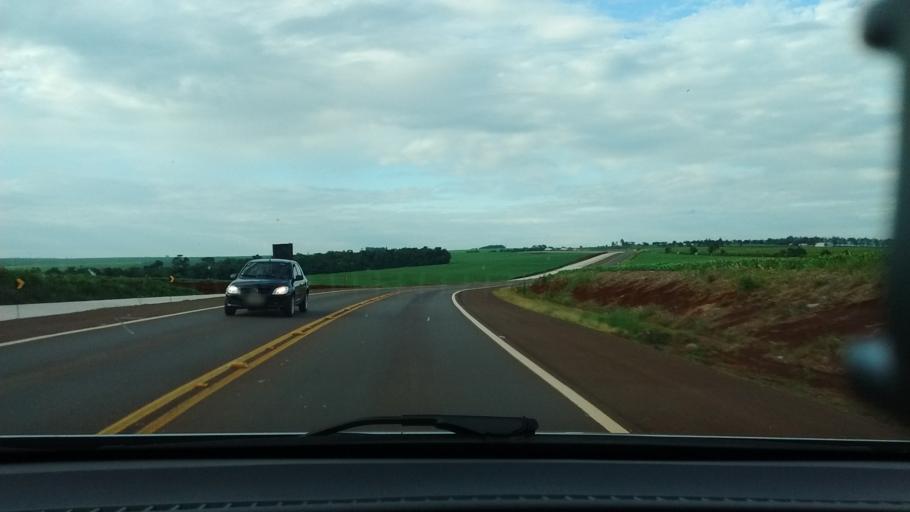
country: BR
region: Parana
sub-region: Cascavel
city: Cascavel
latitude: -25.0313
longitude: -53.5486
